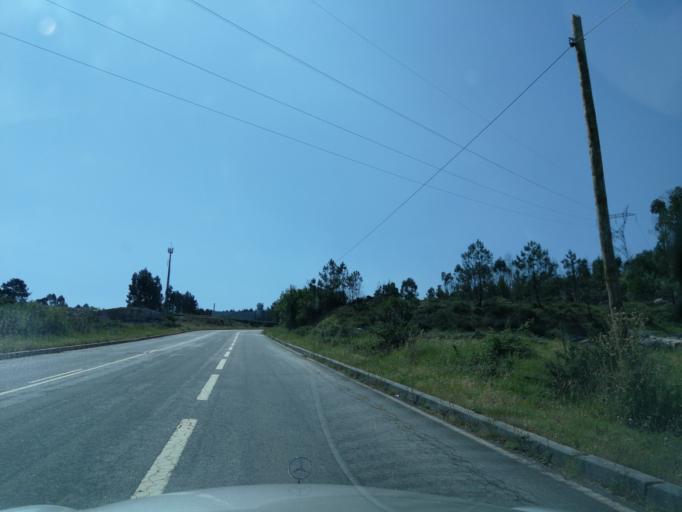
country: PT
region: Braga
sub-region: Braga
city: Adaufe
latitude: 41.5598
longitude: -8.3559
